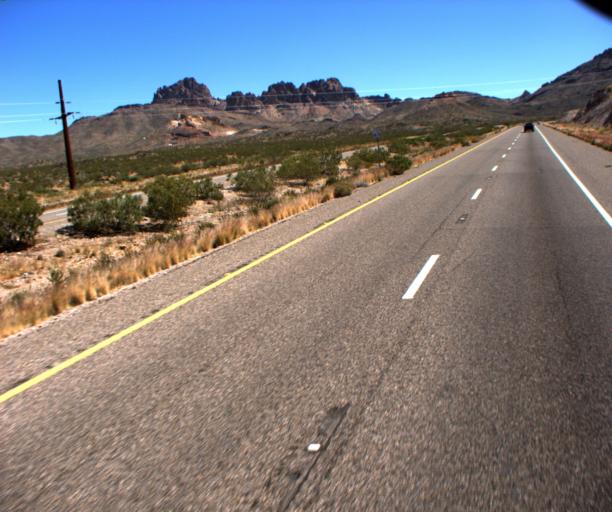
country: US
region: Nevada
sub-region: Clark County
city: Laughlin
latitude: 35.1977
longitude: -114.4280
